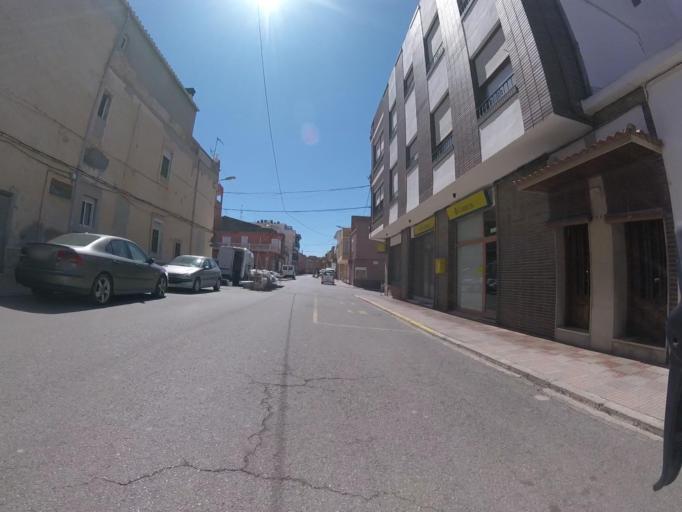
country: ES
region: Valencia
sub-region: Provincia de Castello
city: Cabanes
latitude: 40.1566
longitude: 0.0434
